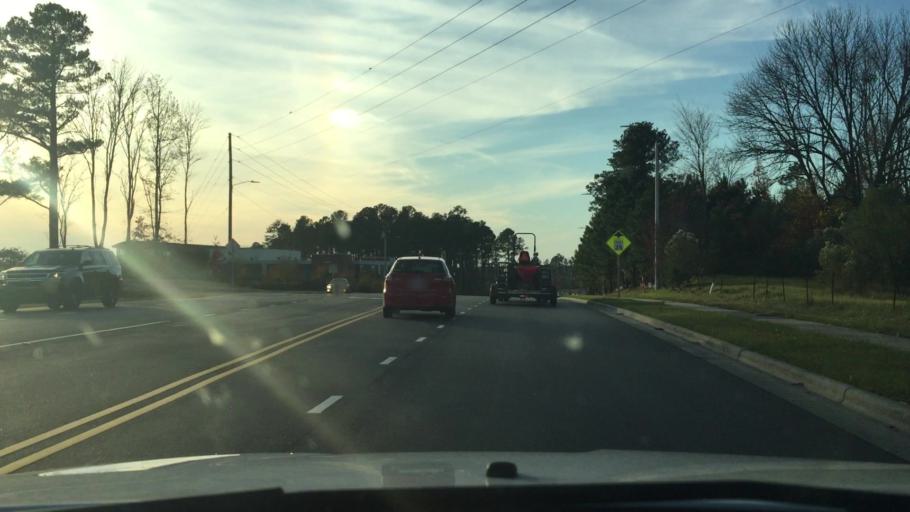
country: US
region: North Carolina
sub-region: Wake County
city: Green Level
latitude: 35.8423
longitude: -78.9009
